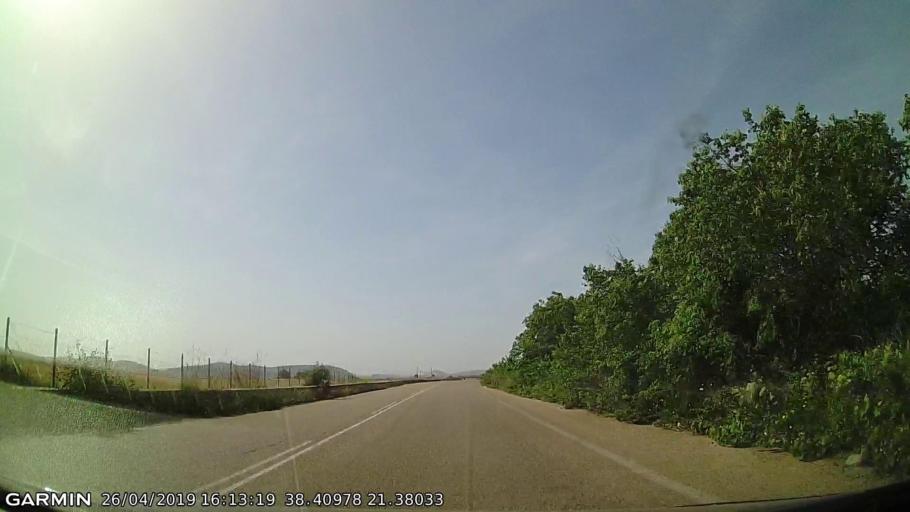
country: GR
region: West Greece
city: Aitoliko
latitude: 38.4098
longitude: 21.3802
